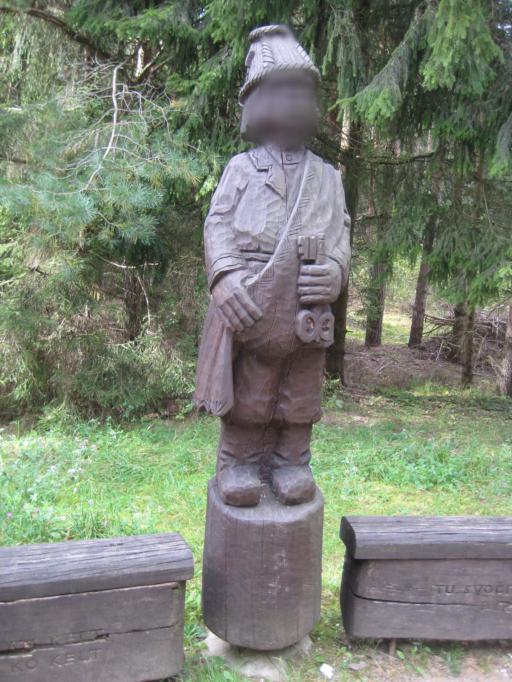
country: LT
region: Utenos apskritis
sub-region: Utena
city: Utena
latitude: 55.5172
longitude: 25.6305
